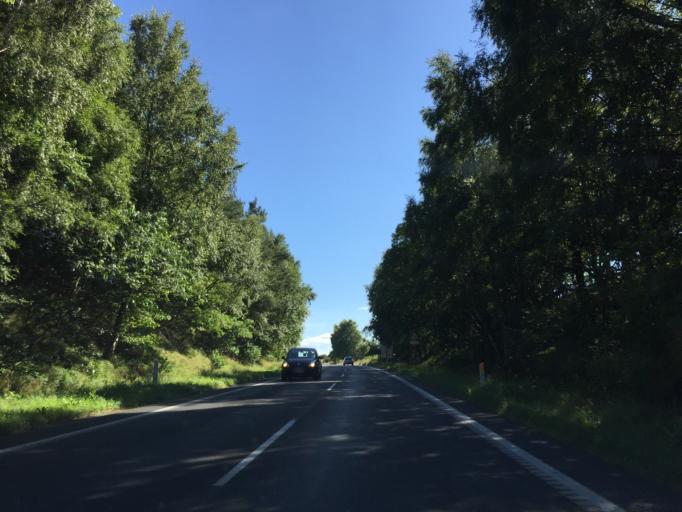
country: DK
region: Central Jutland
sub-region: Viborg Kommune
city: Bjerringbro
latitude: 56.3607
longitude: 9.6743
